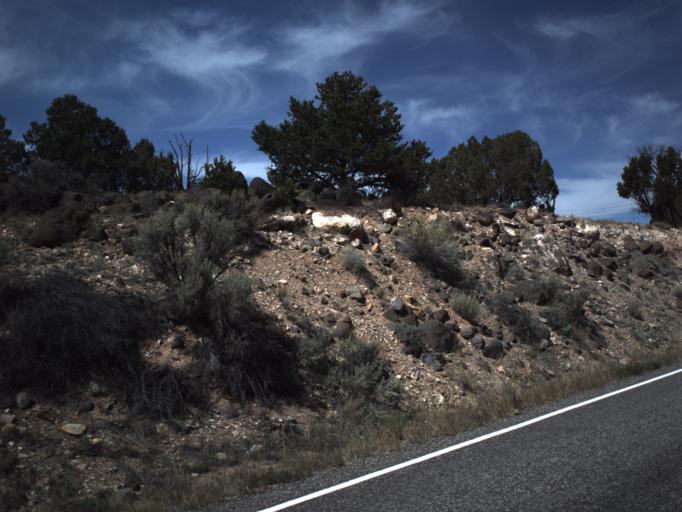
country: US
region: Utah
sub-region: Wayne County
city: Loa
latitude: 38.2617
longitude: -111.3758
